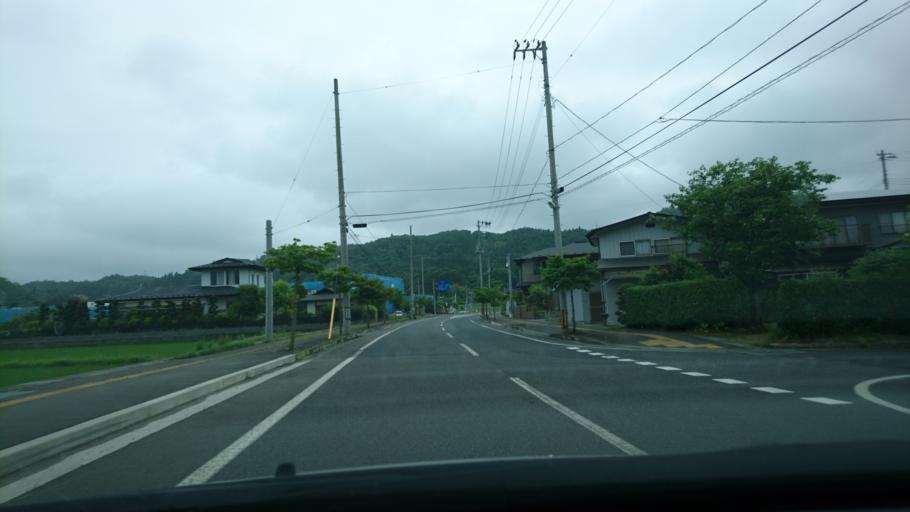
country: JP
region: Iwate
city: Ichinoseki
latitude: 38.9393
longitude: 141.0829
